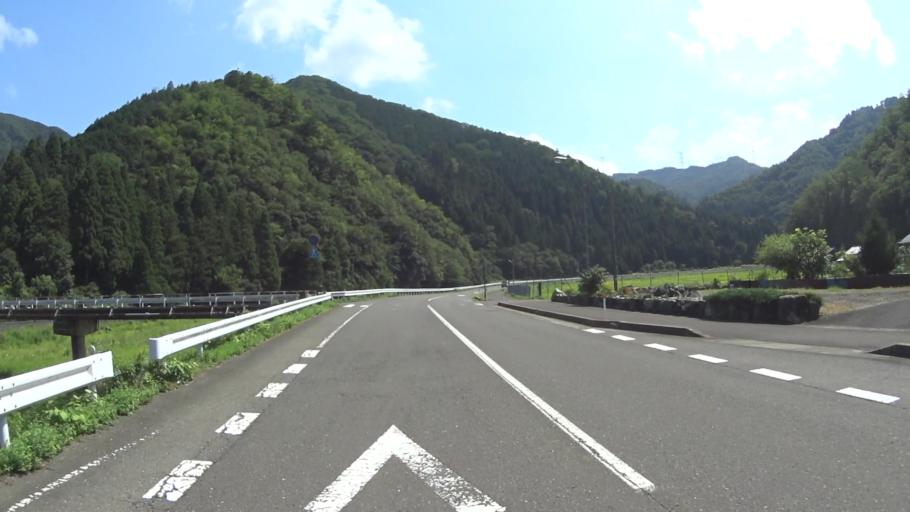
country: JP
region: Fukui
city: Obama
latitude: 35.4024
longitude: 135.6284
